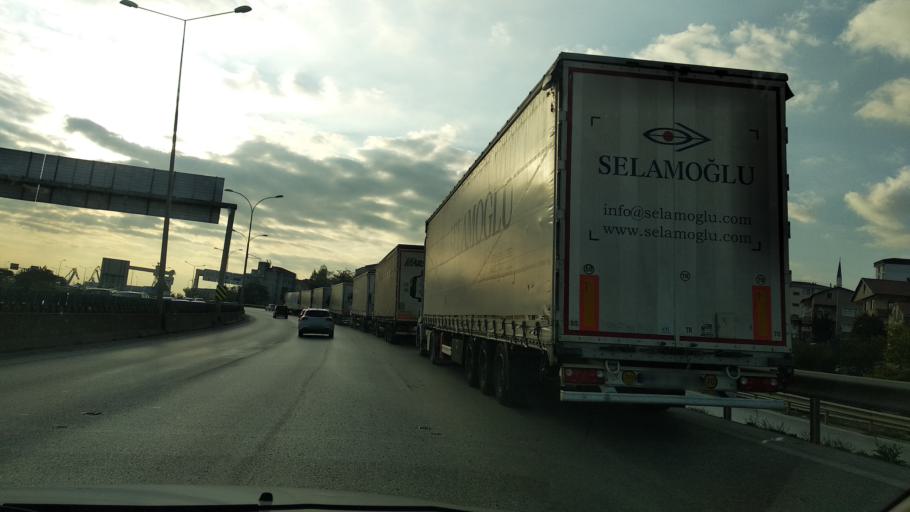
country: TR
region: Istanbul
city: Pendik
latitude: 40.8694
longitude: 29.2773
